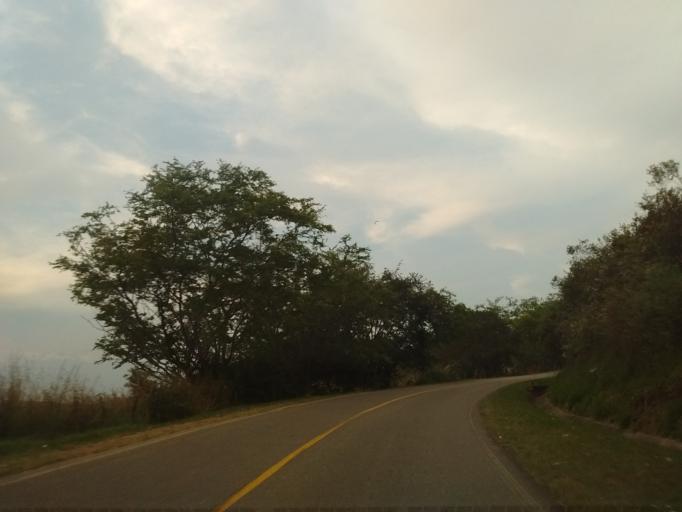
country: CO
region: Cauca
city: Caloto
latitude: 3.0681
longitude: -76.3542
